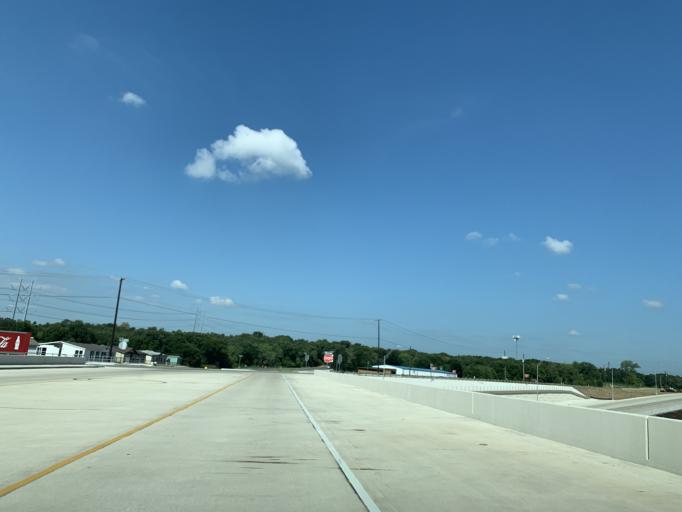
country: US
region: Texas
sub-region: Tarrant County
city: Lakeside
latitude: 32.8594
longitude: -97.5179
